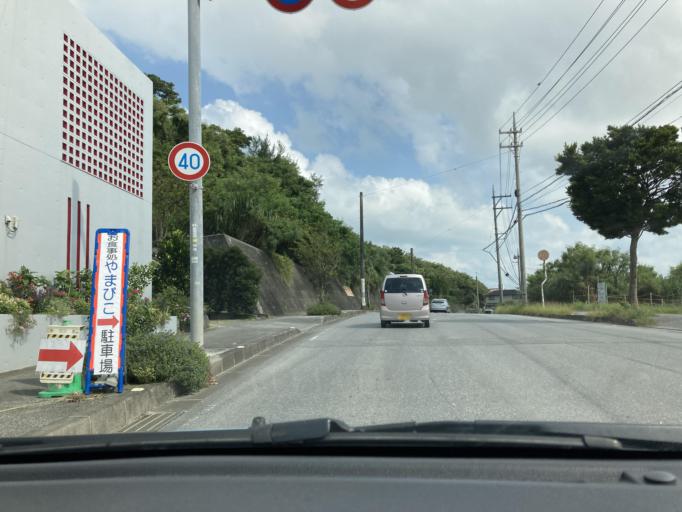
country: JP
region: Okinawa
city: Ginowan
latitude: 26.2414
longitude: 127.7553
